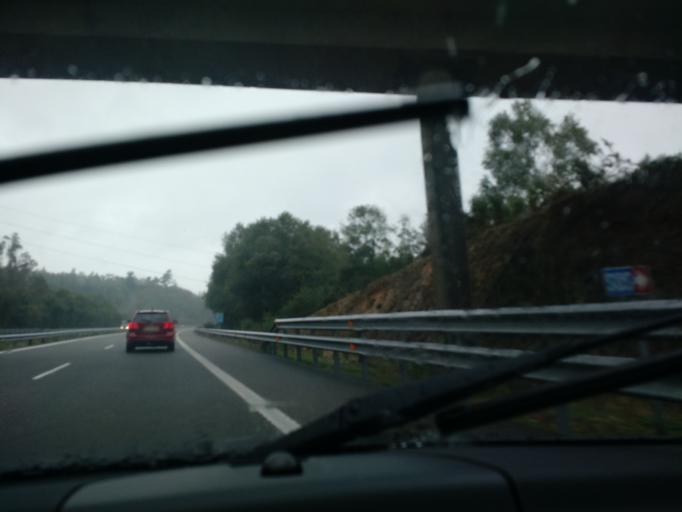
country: ES
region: Galicia
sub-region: Provincia da Coruna
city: Abegondo
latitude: 43.1590
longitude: -8.3265
